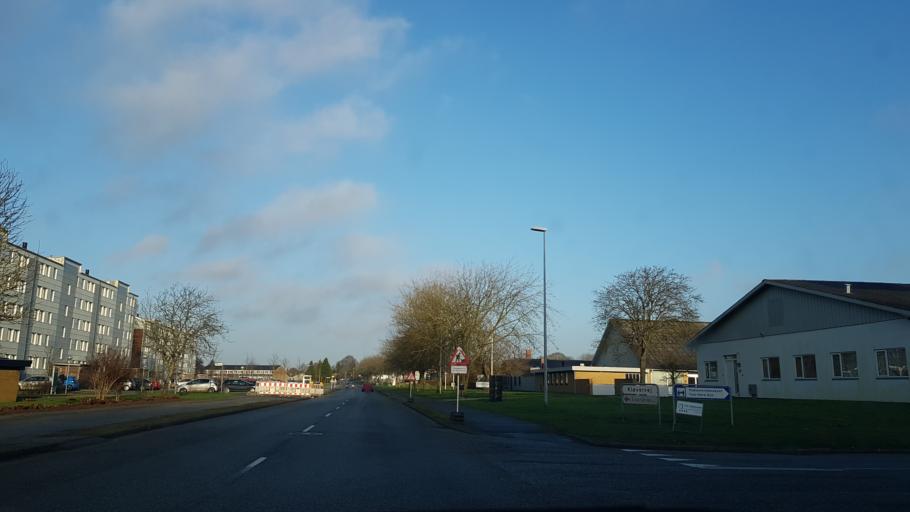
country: DK
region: South Denmark
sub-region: Haderslev Kommune
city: Haderslev
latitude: 55.2333
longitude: 9.4954
